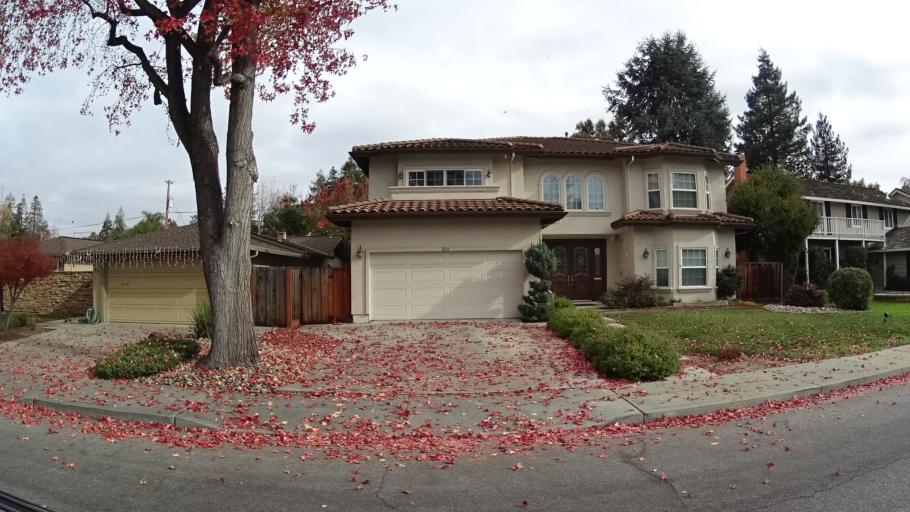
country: US
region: California
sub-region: Santa Clara County
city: Sunnyvale
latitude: 37.3634
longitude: -122.0408
